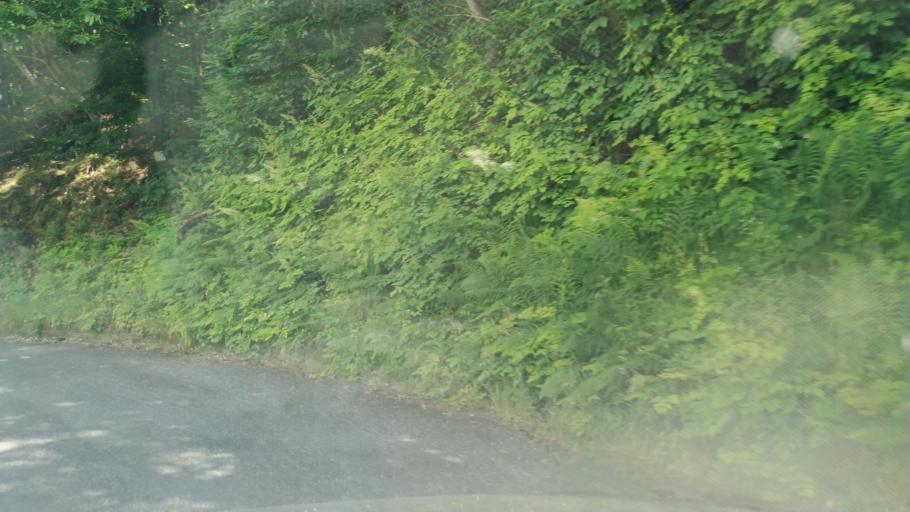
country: IT
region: Piedmont
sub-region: Provincia di Torino
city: Cintano
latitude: 45.4207
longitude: 7.7016
